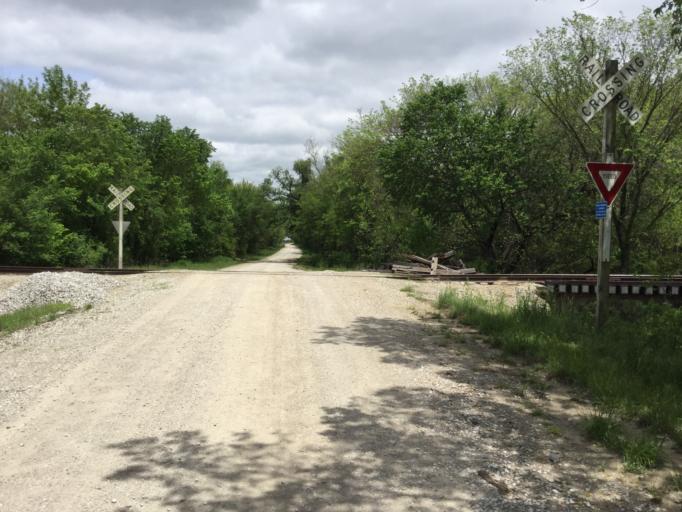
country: US
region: Kansas
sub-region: Labette County
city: Altamont
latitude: 37.1949
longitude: -95.3224
